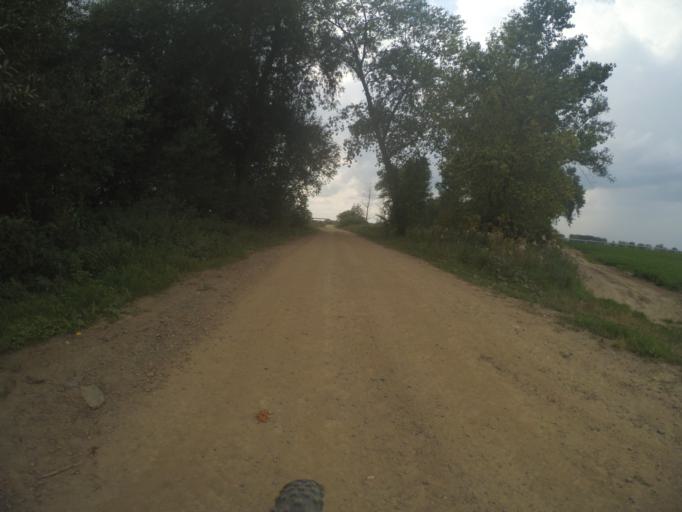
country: CZ
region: Central Bohemia
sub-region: Okres Melnik
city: Melnik
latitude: 50.3110
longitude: 14.4497
